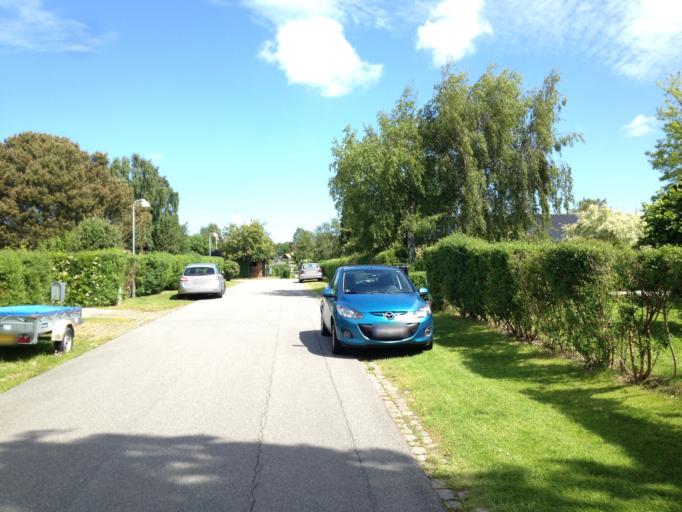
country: DK
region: Capital Region
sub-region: Fredensborg Kommune
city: Niva
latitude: 55.9323
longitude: 12.4918
